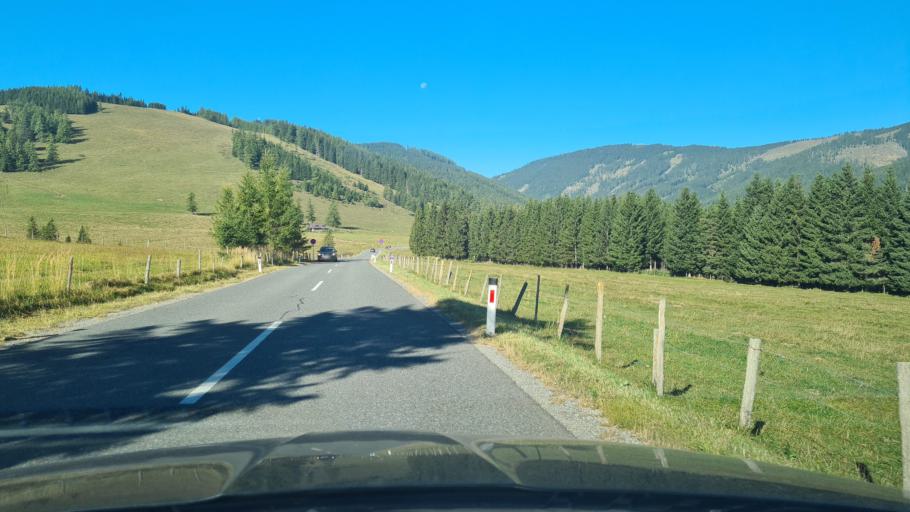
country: AT
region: Styria
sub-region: Politischer Bezirk Weiz
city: Passail
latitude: 47.3449
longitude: 15.4725
